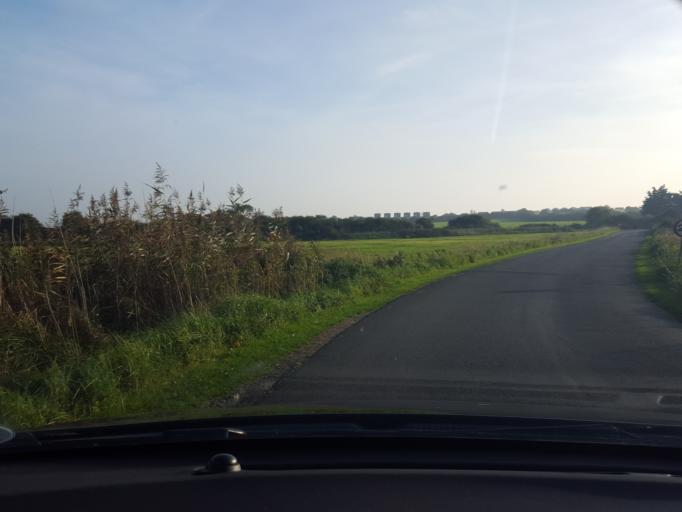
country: GB
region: England
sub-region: Essex
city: Walton-on-the-Naze
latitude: 51.8578
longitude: 1.2592
